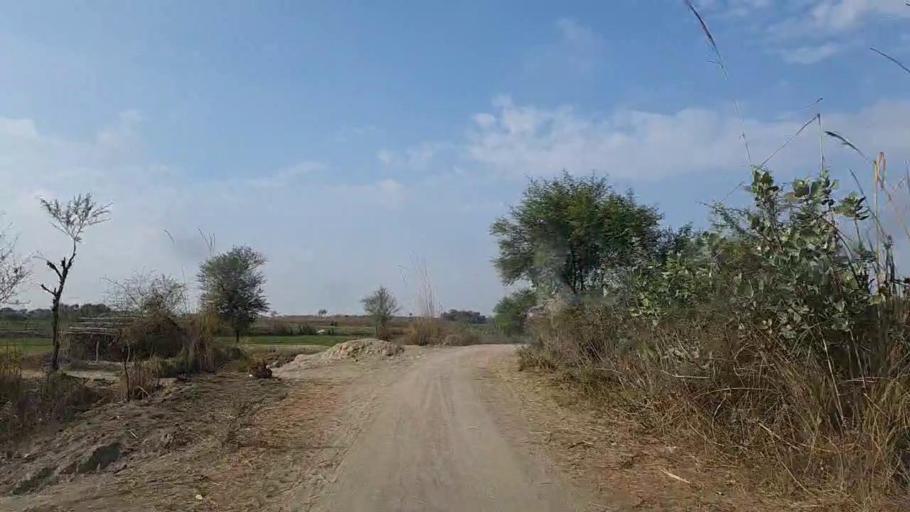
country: PK
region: Sindh
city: Sanghar
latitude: 26.2547
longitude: 69.0101
